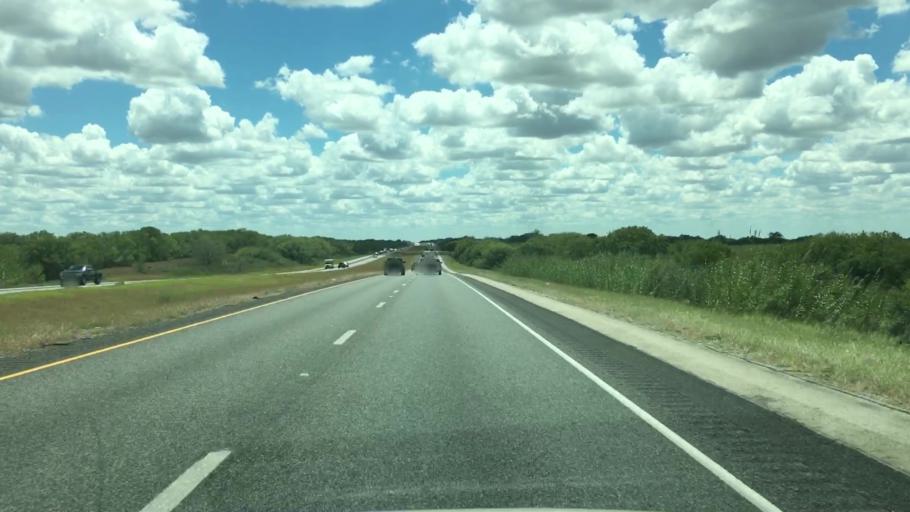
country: US
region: Texas
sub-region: Atascosa County
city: Pleasanton
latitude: 29.0860
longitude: -98.4331
